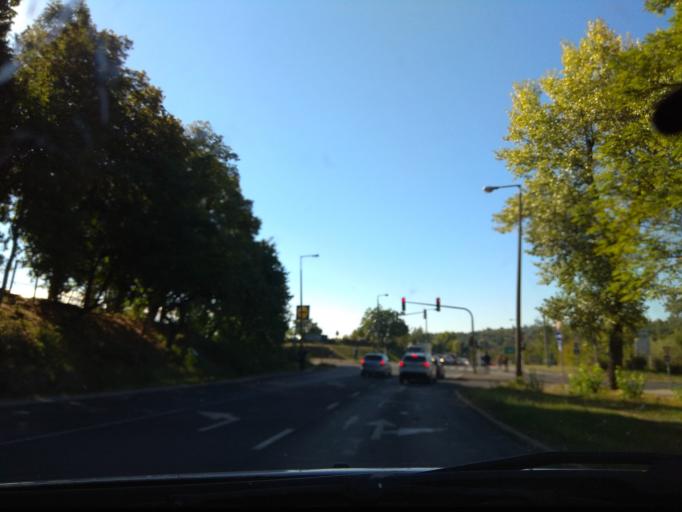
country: HU
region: Borsod-Abauj-Zemplen
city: Miskolc
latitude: 48.0783
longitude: 20.7722
